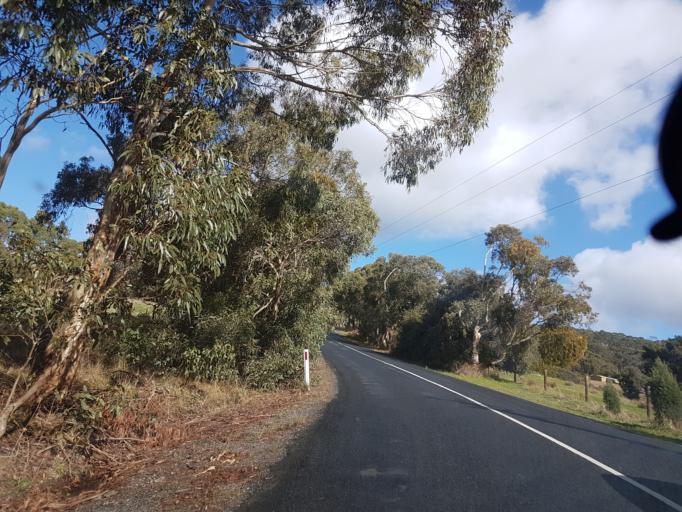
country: AU
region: South Australia
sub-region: Adelaide Hills
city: Heathfield
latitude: -35.0428
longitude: 138.7080
